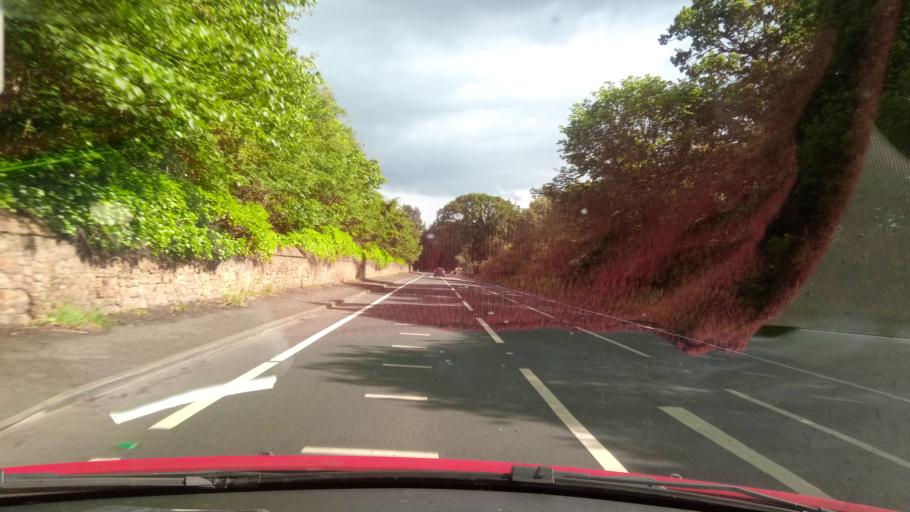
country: GB
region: Scotland
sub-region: Fife
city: Pathhead
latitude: 55.8792
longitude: -2.9869
